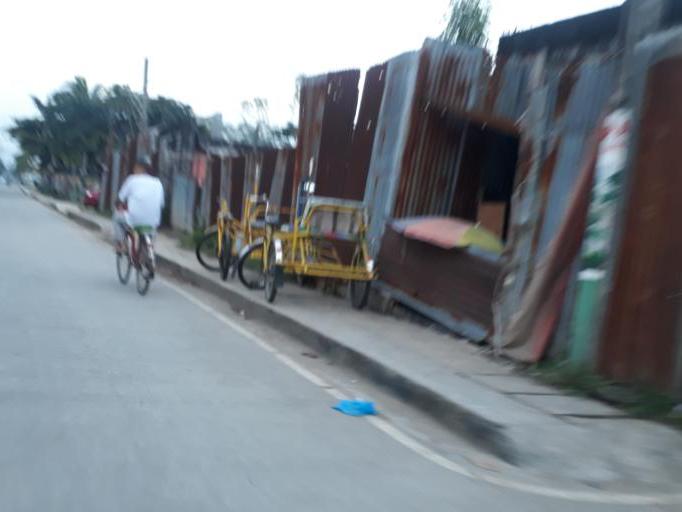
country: PH
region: Central Luzon
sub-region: Province of Bulacan
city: Obando
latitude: 14.7098
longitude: 120.9516
